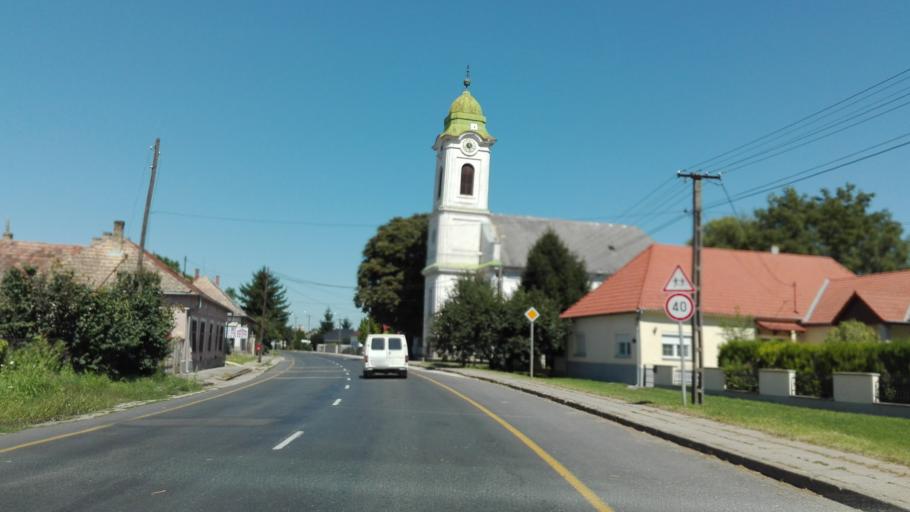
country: HU
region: Fejer
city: Mezoszilas
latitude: 46.8098
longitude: 18.4841
